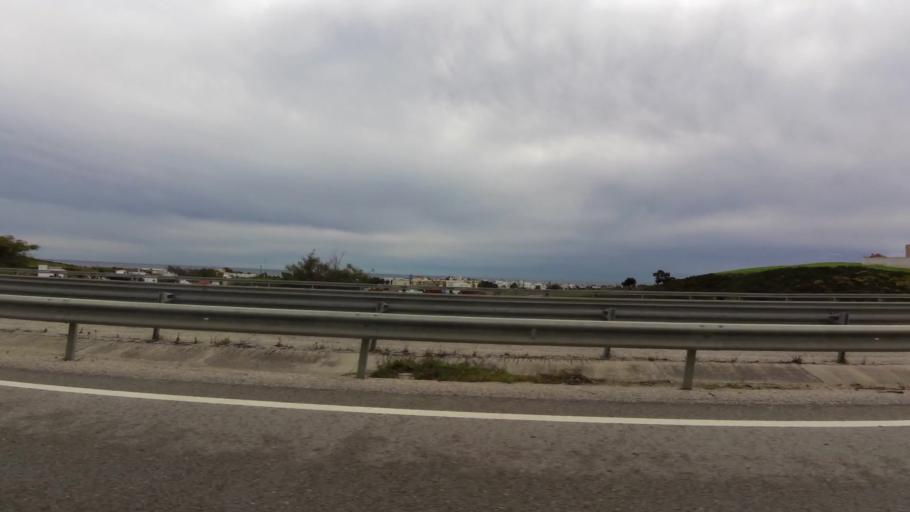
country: MA
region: Tanger-Tetouan
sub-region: Tetouan
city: Martil
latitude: 35.7341
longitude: -5.3531
